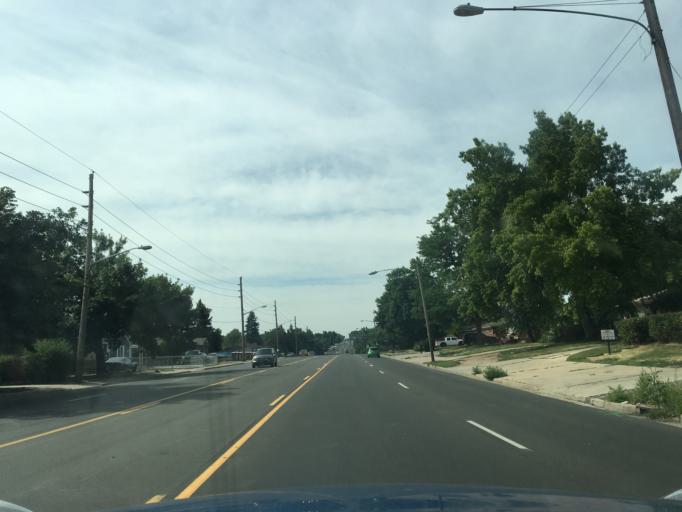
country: US
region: Colorado
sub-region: Jefferson County
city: Lakewood
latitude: 39.6872
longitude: -105.0533
